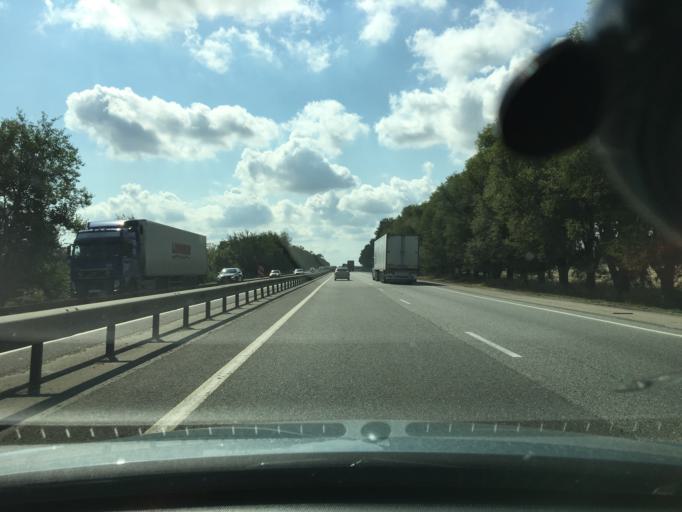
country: RU
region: Krasnodarskiy
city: Krasnoye
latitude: 46.6925
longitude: 39.6519
